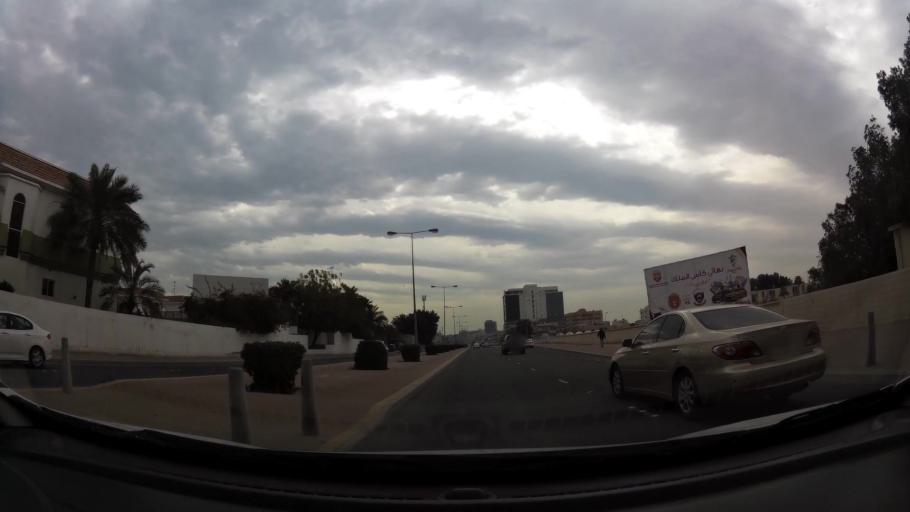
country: BH
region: Manama
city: Manama
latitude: 26.2119
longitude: 50.5918
